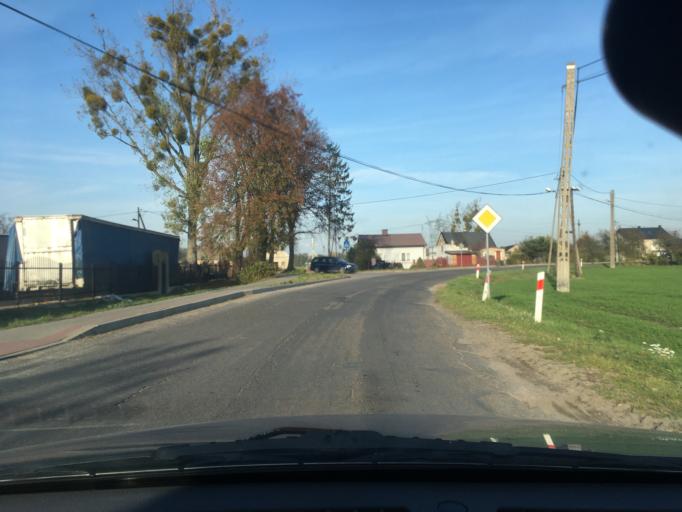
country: PL
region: Masovian Voivodeship
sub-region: Powiat plocki
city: Mala Wies
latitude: 52.4627
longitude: 20.1093
